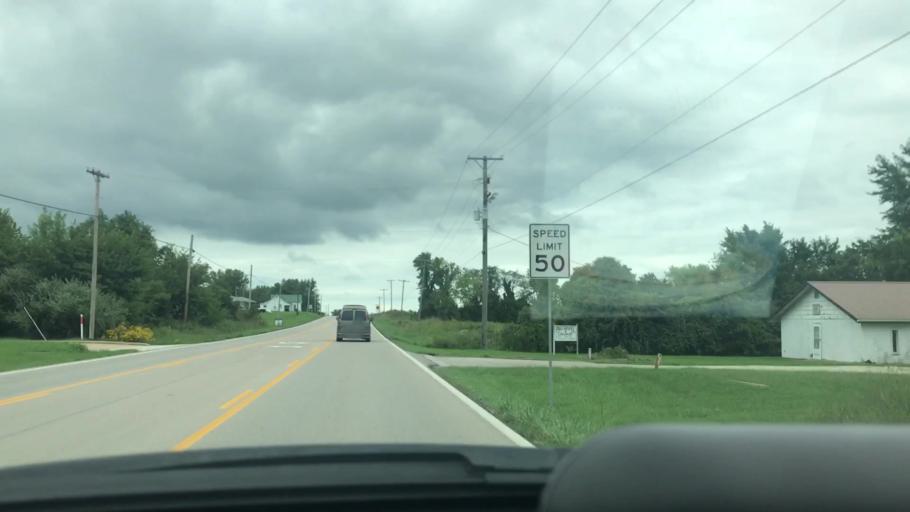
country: US
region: Missouri
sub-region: Dallas County
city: Buffalo
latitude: 37.6493
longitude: -93.1039
